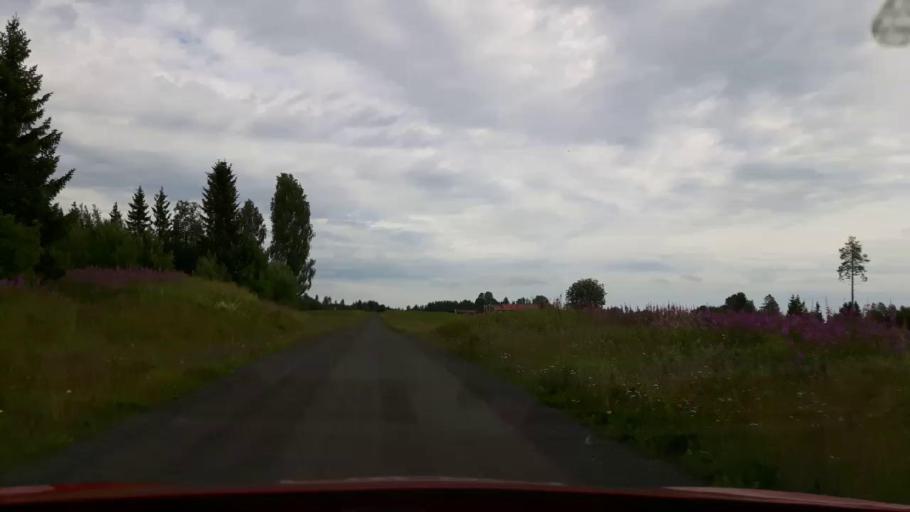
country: SE
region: Jaemtland
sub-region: OEstersunds Kommun
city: Lit
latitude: 63.4118
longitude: 15.2434
